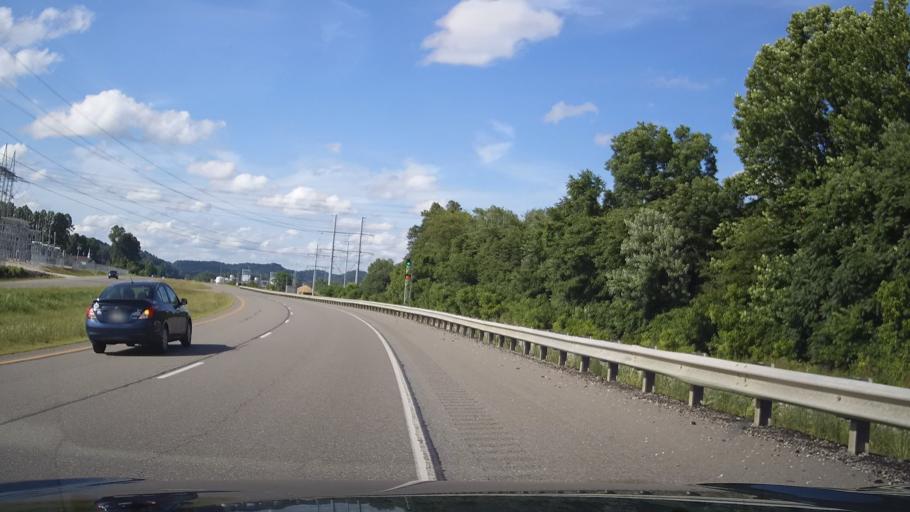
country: US
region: Kentucky
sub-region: Lawrence County
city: Louisa
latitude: 38.1795
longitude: -82.6090
